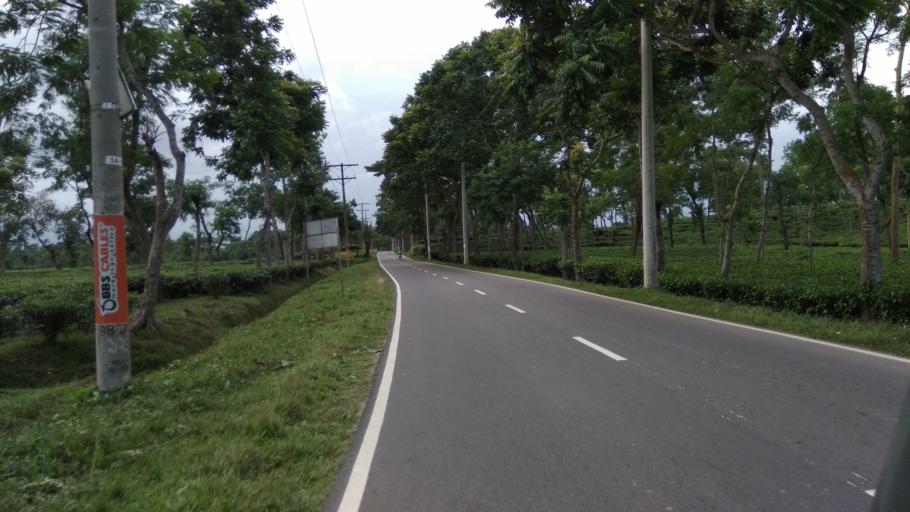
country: IN
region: Tripura
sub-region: Dhalai
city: Kamalpur
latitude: 24.3015
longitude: 91.7530
